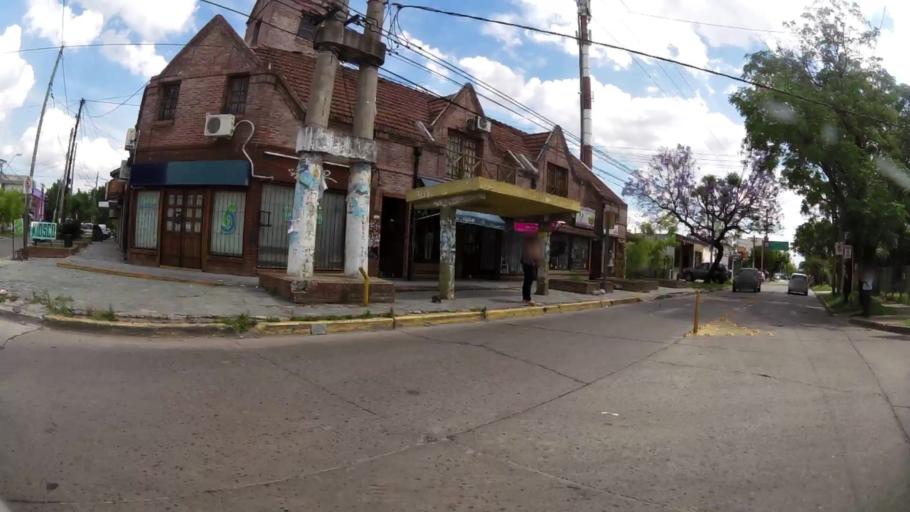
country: AR
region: Buenos Aires
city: Ituzaingo
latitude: -34.6482
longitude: -58.6645
